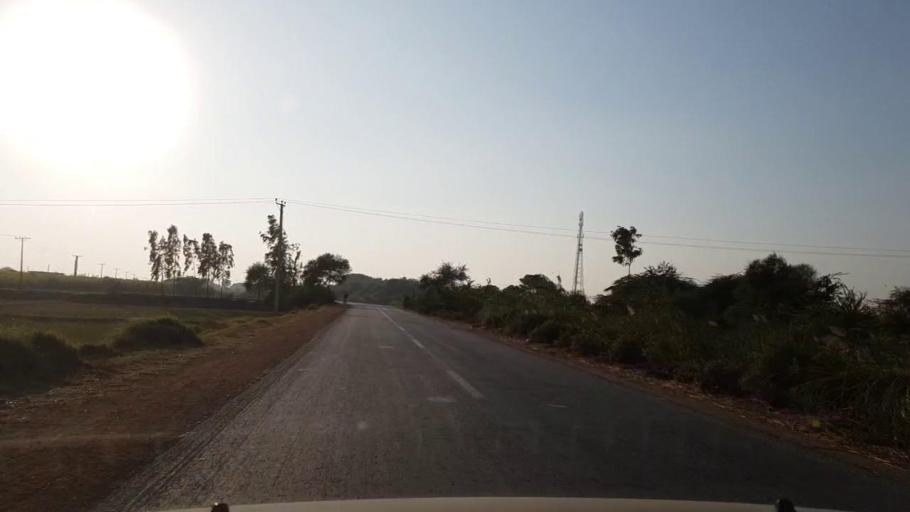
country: PK
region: Sindh
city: Mirpur Batoro
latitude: 24.6863
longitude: 68.1678
